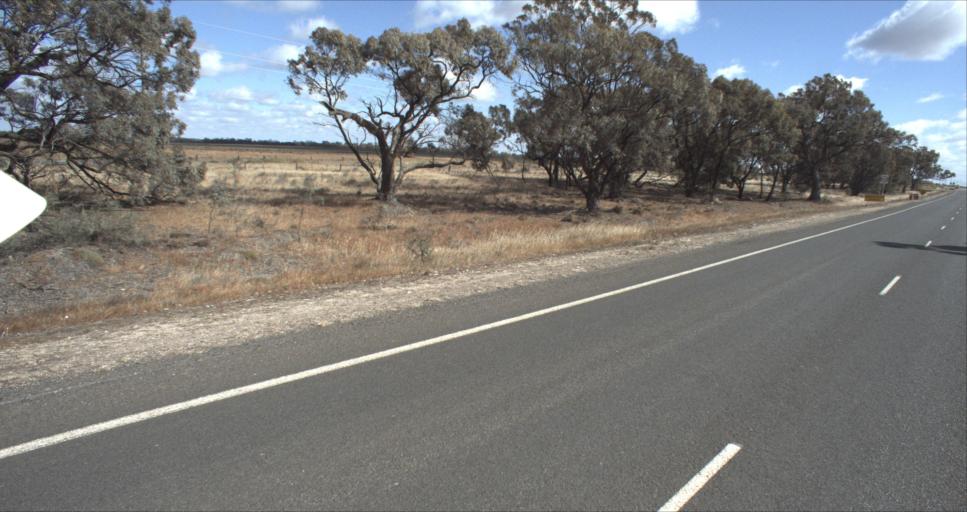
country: AU
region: New South Wales
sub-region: Murrumbidgee Shire
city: Darlington Point
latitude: -34.5564
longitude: 146.1698
